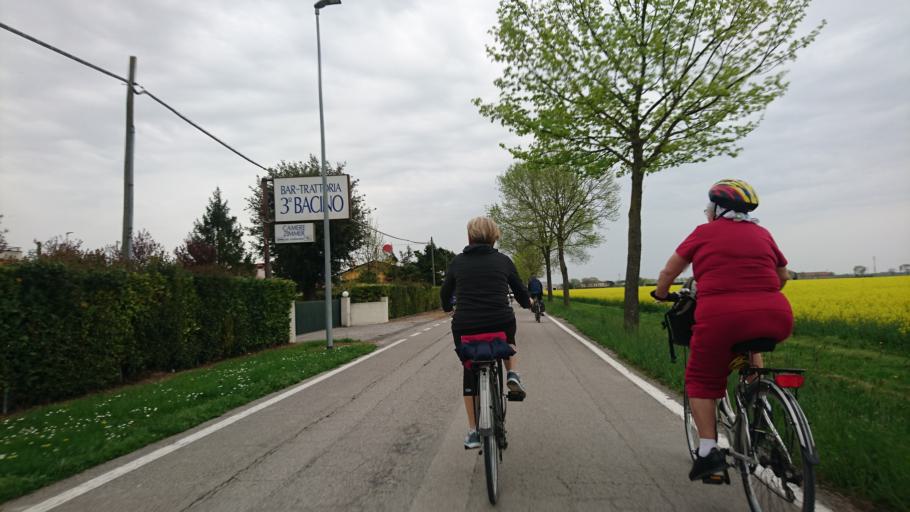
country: IT
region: Veneto
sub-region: Provincia di Venezia
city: Bibione
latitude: 45.6648
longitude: 12.9942
